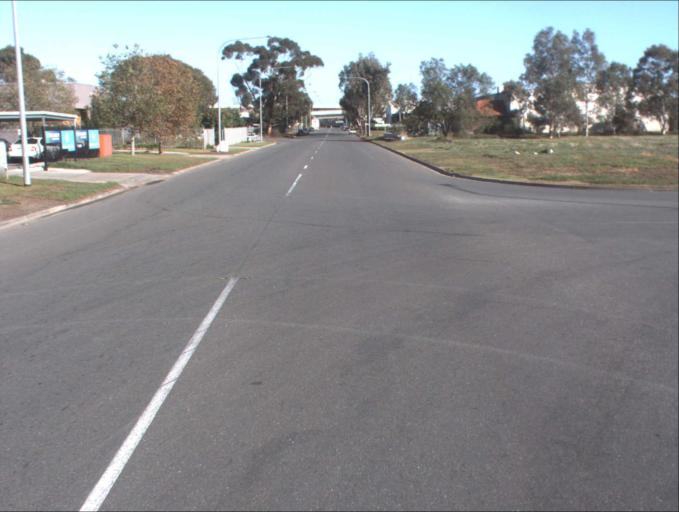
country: AU
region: South Australia
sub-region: Port Adelaide Enfield
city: Blair Athol
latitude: -34.8468
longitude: 138.5704
